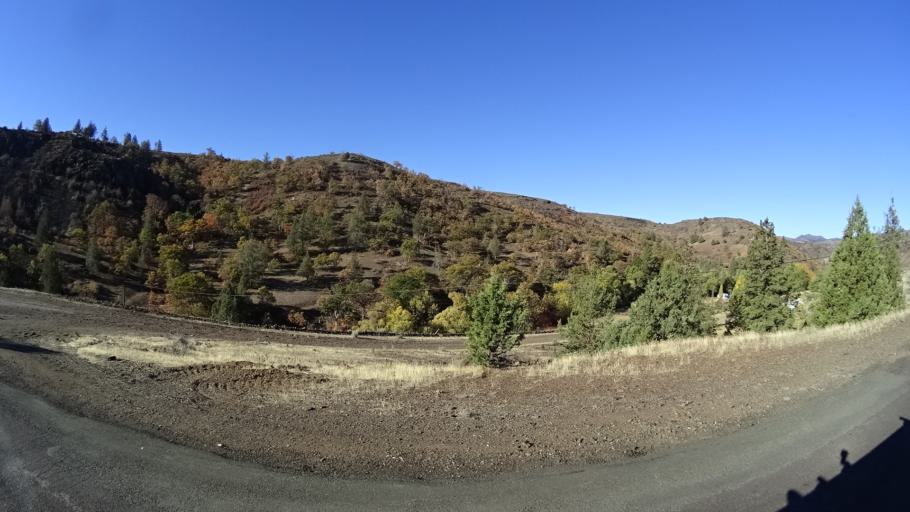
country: US
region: California
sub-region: Siskiyou County
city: Montague
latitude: 41.9378
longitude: -122.4448
